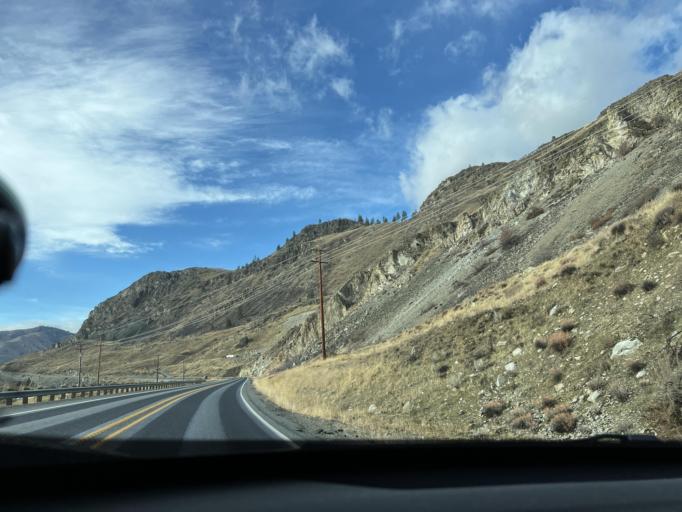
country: US
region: Washington
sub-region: Chelan County
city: Chelan
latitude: 47.8550
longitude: -119.9598
